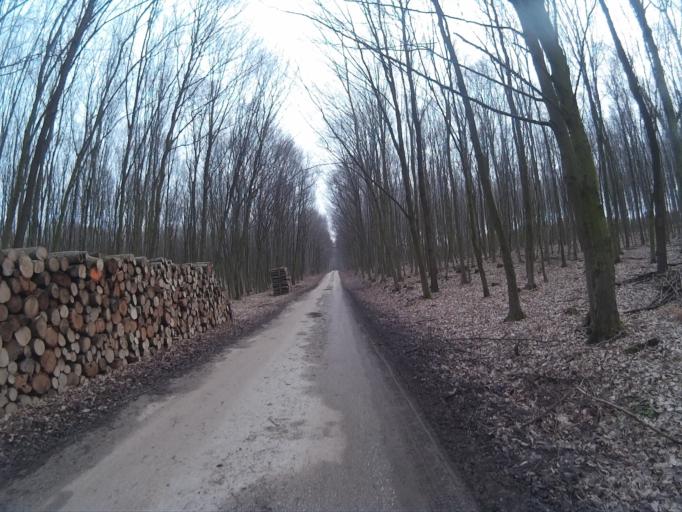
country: HU
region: Komarom-Esztergom
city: Tatabanya
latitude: 47.5801
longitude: 18.4547
